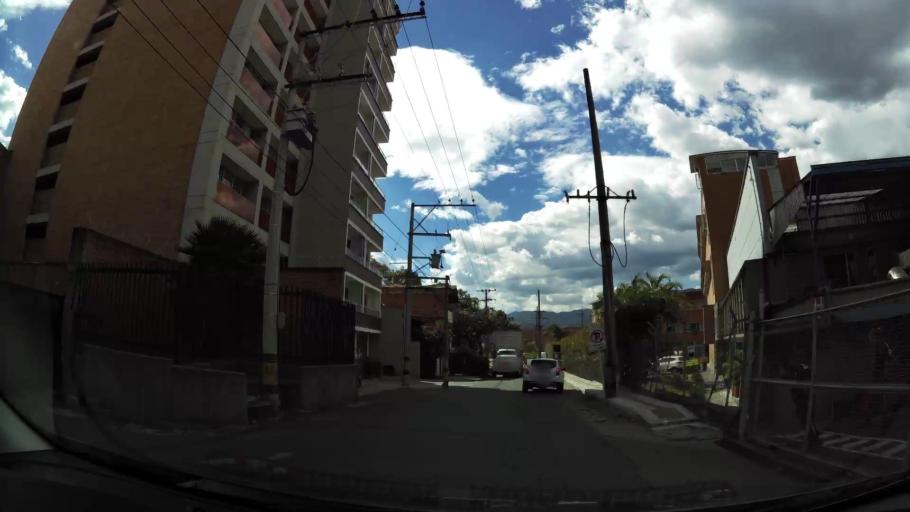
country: CO
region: Antioquia
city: Sabaneta
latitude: 6.1560
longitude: -75.6107
